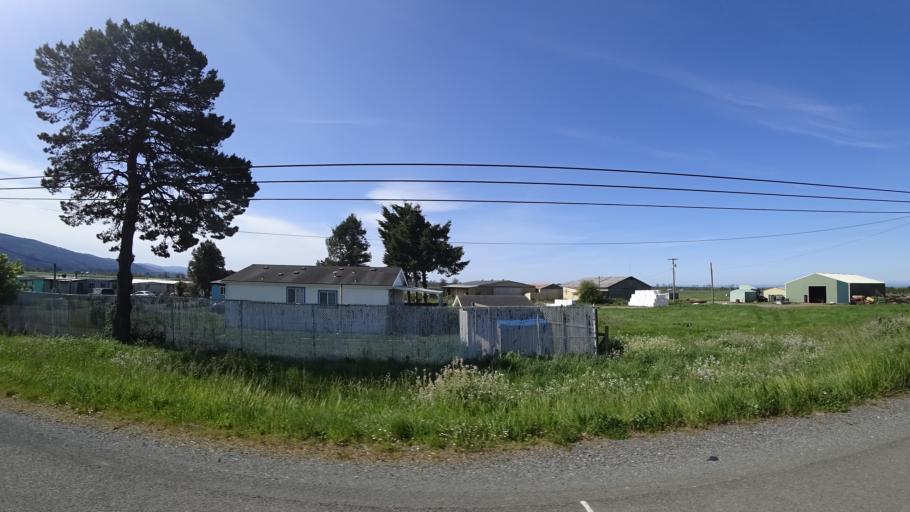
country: US
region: Oregon
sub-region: Curry County
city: Harbor
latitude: 41.9345
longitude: -124.1685
